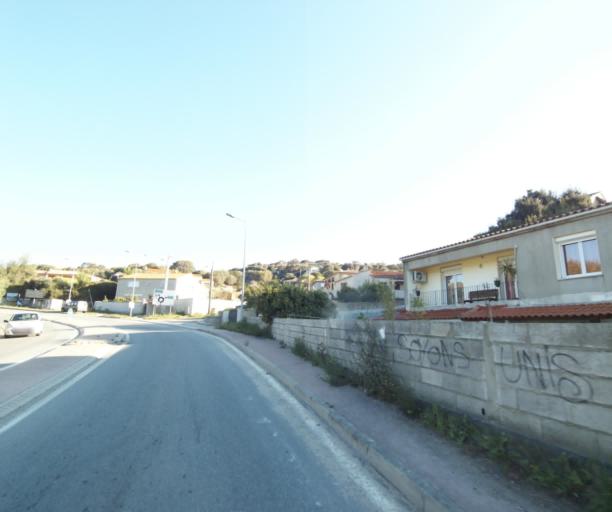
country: FR
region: Corsica
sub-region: Departement de la Corse-du-Sud
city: Propriano
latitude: 41.6682
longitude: 8.9213
